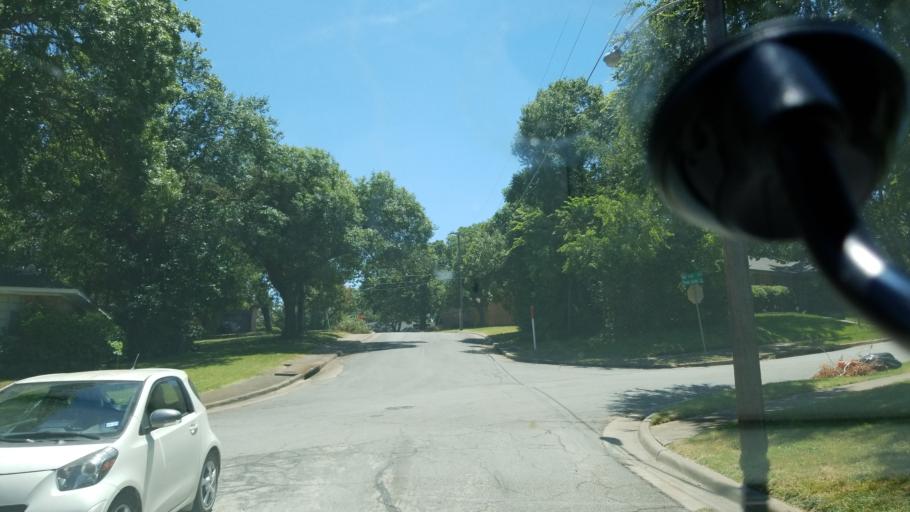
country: US
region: Texas
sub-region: Dallas County
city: Cockrell Hill
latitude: 32.6891
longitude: -96.8359
